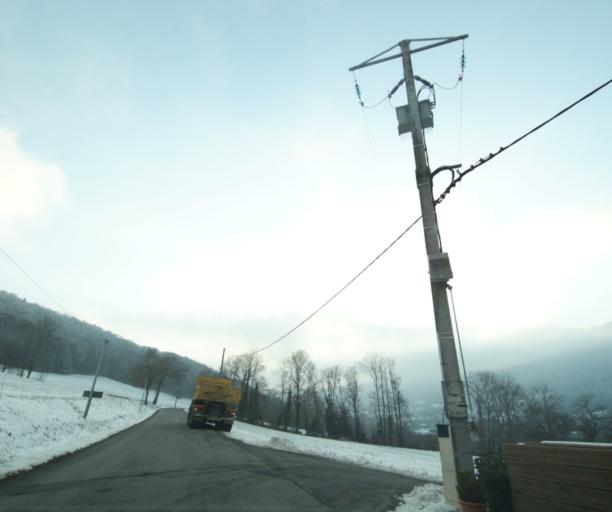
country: FR
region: Rhone-Alpes
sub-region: Departement de la Haute-Savoie
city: Monnetier-Mornex
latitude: 46.1362
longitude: 6.2226
